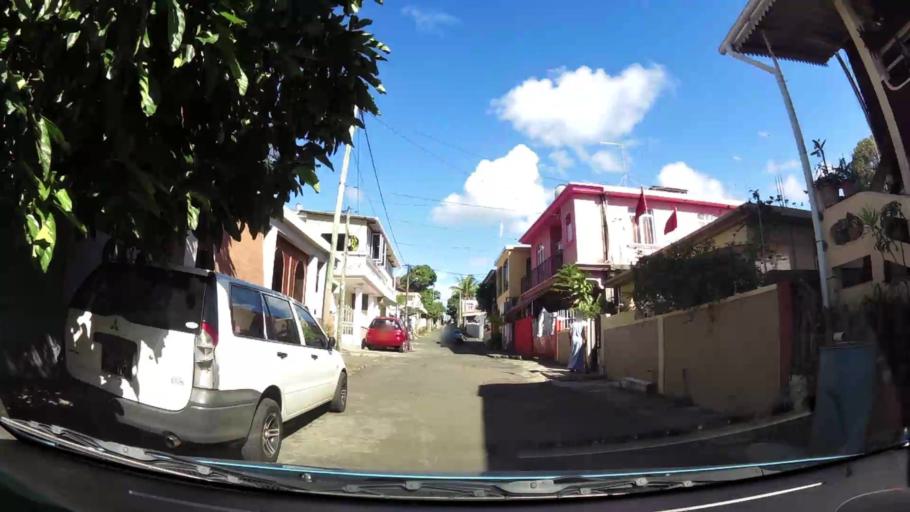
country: MU
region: Grand Port
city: Mahebourg
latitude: -20.4068
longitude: 57.7029
